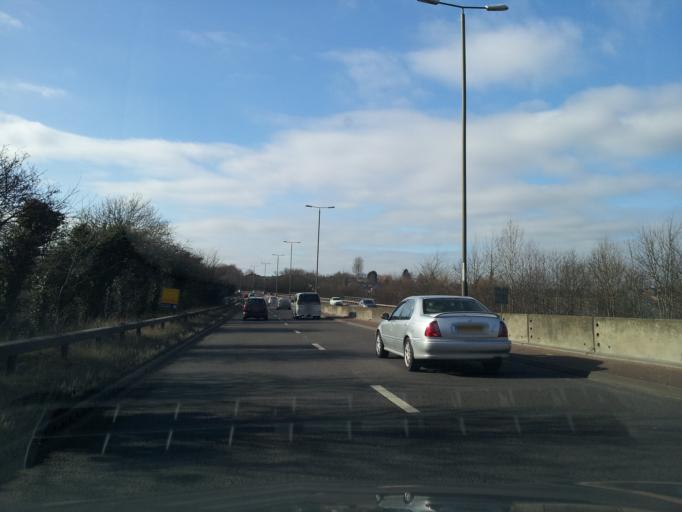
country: GB
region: England
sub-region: Derbyshire
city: Long Eaton
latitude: 52.9192
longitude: -1.2845
